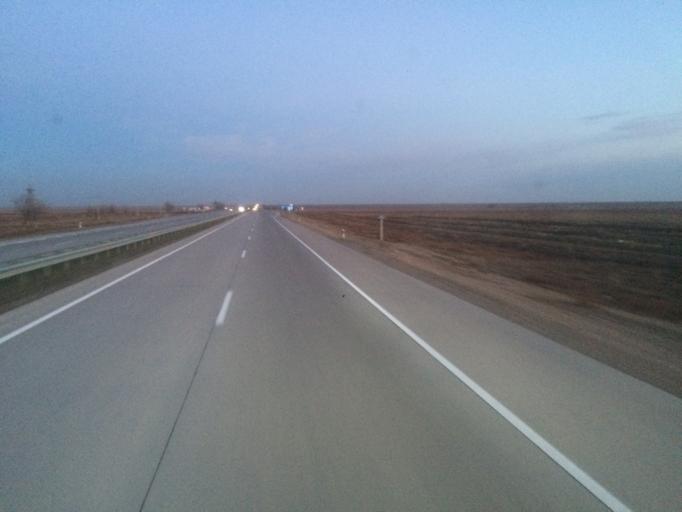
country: KZ
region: Ongtustik Qazaqstan
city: Temirlanovka
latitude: 42.8475
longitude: 69.0901
